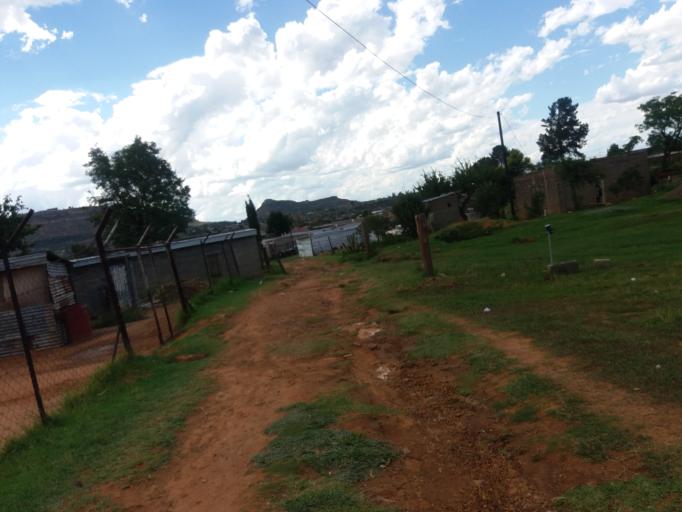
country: LS
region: Maseru
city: Maseru
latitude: -29.3685
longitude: 27.5060
